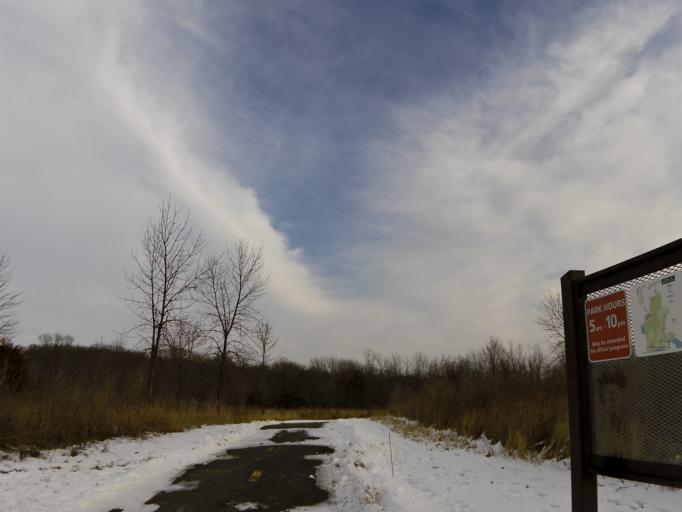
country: US
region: Minnesota
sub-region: Scott County
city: Prior Lake
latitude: 44.7164
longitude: -93.4719
